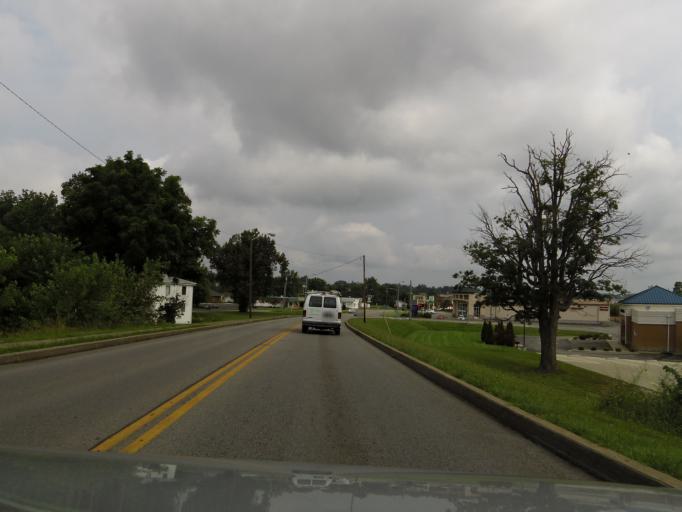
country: US
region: Kentucky
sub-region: Hopkins County
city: Madisonville
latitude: 37.3392
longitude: -87.4979
